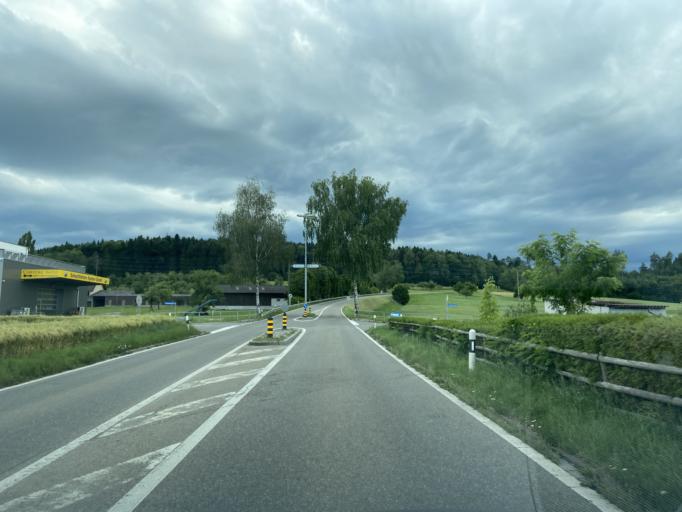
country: CH
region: Thurgau
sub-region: Frauenfeld District
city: Matzingen
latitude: 47.5046
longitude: 8.9198
